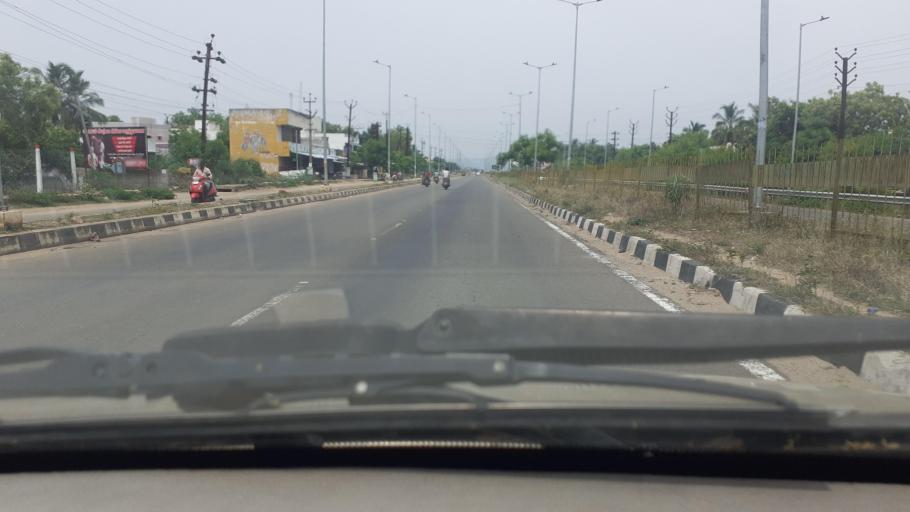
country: IN
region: Tamil Nadu
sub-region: Tirunelveli Kattabo
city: Tirunelveli
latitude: 8.7138
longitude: 77.7747
